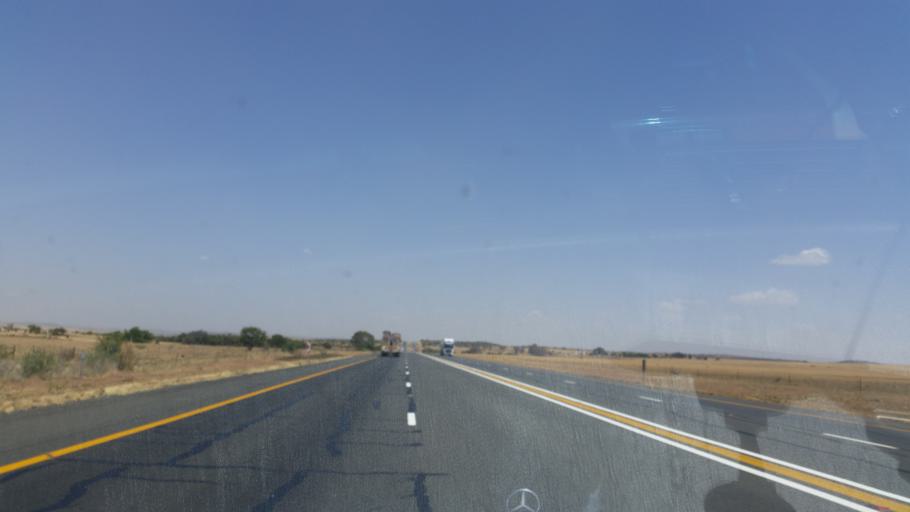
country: ZA
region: Orange Free State
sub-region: Lejweleputswa District Municipality
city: Brandfort
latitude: -28.8955
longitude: 26.4765
